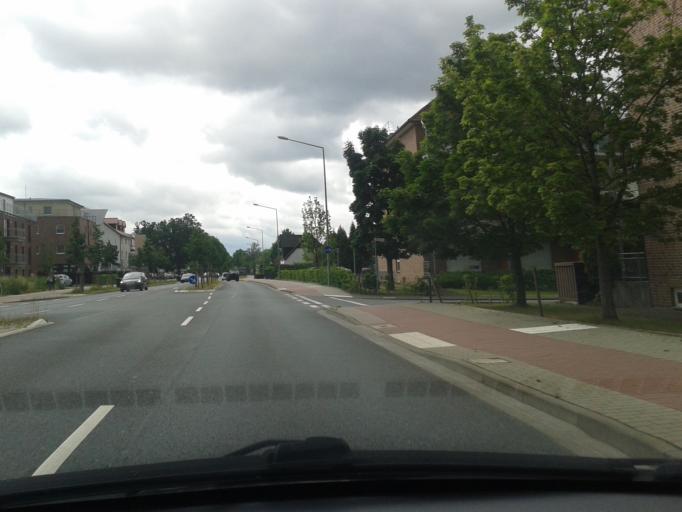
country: DE
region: North Rhine-Westphalia
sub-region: Regierungsbezirk Detmold
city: Paderborn
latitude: 51.7447
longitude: 8.7733
